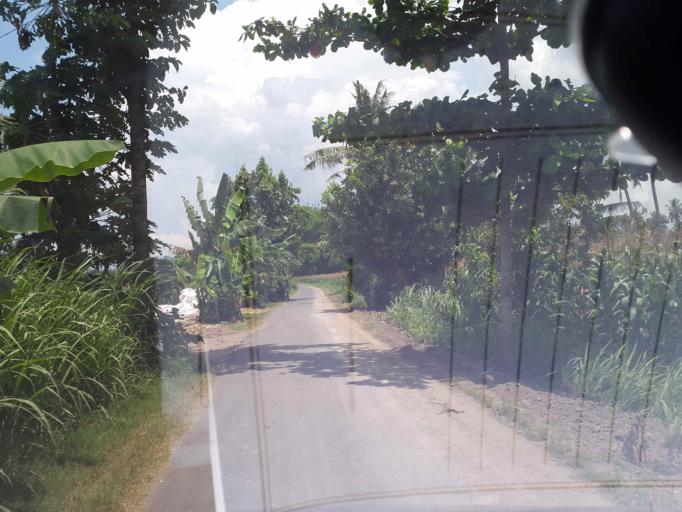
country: ID
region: West Nusa Tenggara
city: Jelateng Timur
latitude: -8.7017
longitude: 116.0808
